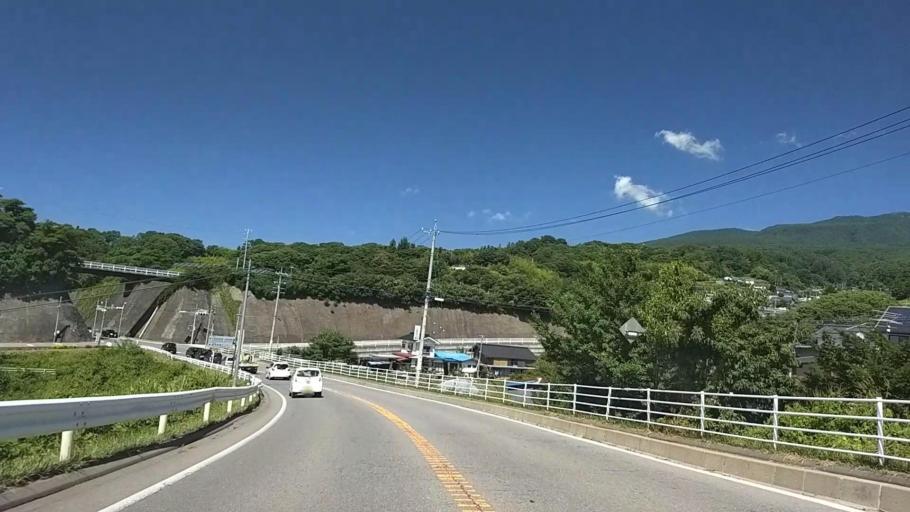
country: JP
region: Nagano
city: Komoro
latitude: 36.3486
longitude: 138.4321
